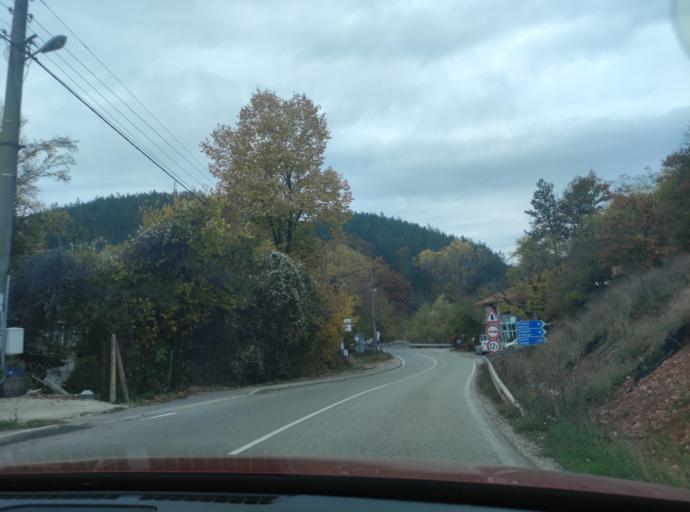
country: BG
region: Sofiya
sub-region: Obshtina Godech
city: Godech
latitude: 42.9749
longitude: 23.1387
